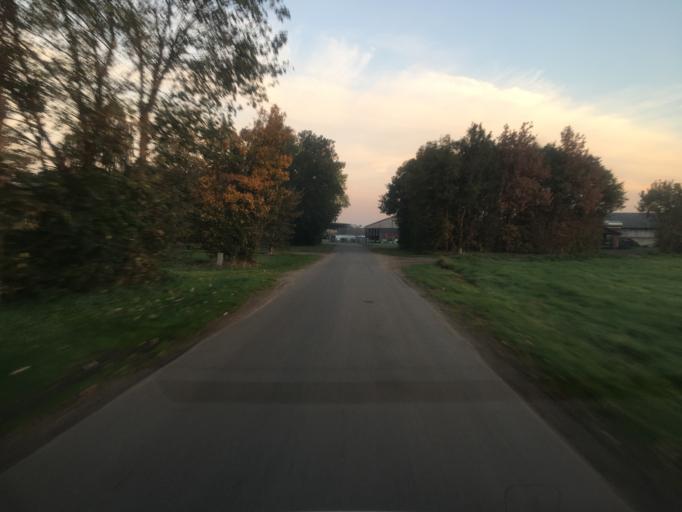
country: DE
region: Schleswig-Holstein
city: Bramstedtlund
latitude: 54.9822
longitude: 9.0658
